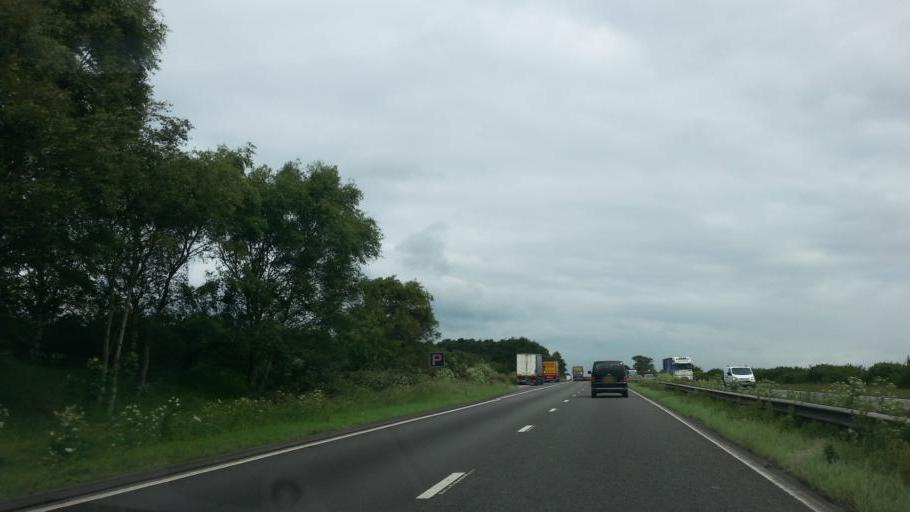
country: GB
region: England
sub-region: Nottinghamshire
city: Bircotes
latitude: 53.3548
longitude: -1.0396
